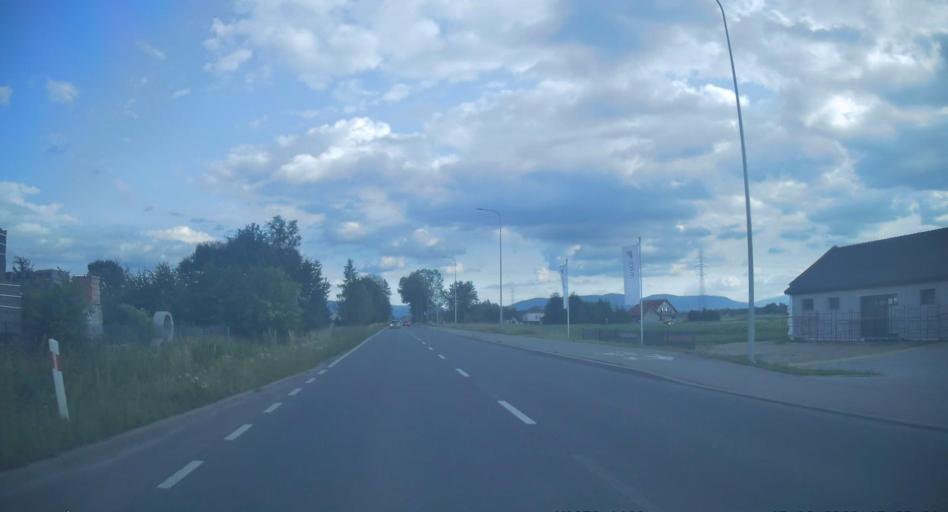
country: PL
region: Lesser Poland Voivodeship
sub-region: Powiat oswiecimski
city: Nowa Wies
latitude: 49.9342
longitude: 19.2118
